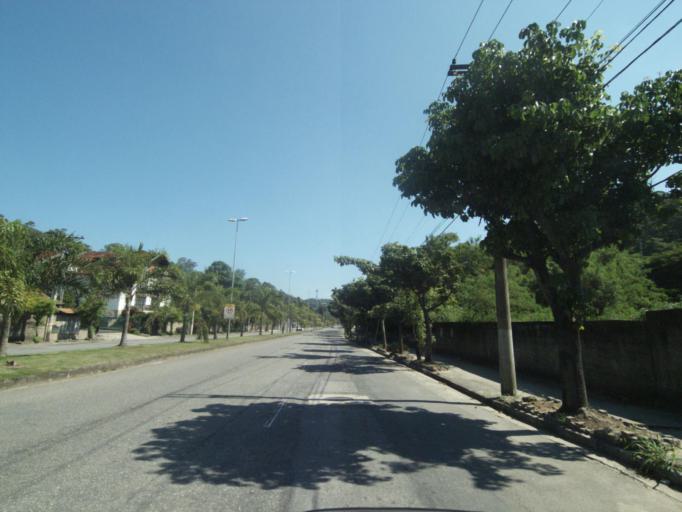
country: BR
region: Rio de Janeiro
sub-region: Sao Goncalo
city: Sao Goncalo
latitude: -22.8904
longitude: -43.0348
